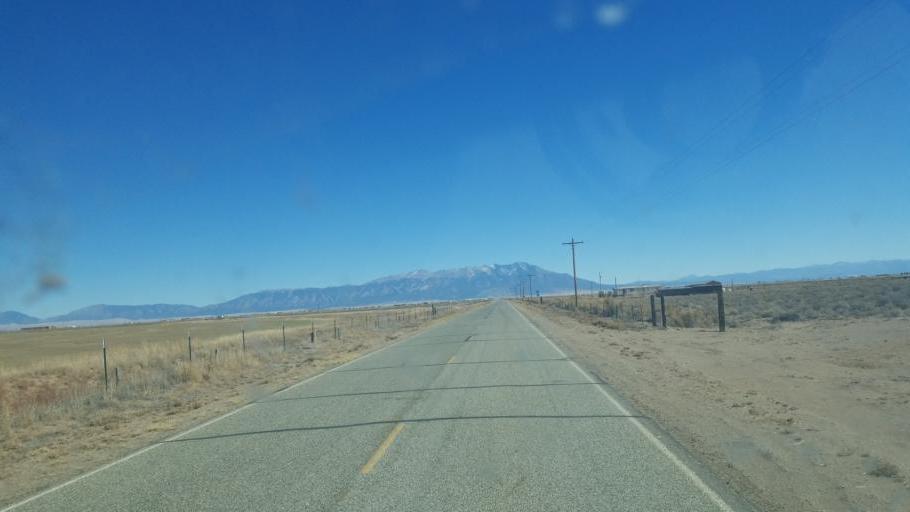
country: US
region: Colorado
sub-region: Alamosa County
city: Alamosa
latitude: 37.5744
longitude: -105.9339
